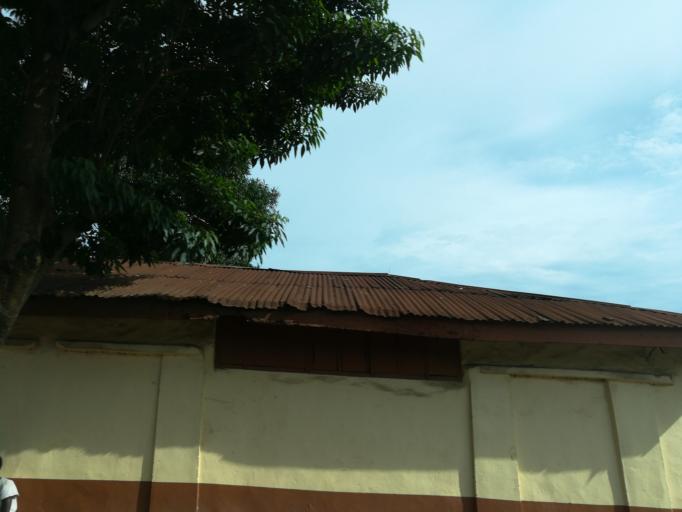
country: NG
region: Lagos
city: Oshodi
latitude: 6.5630
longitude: 3.3466
